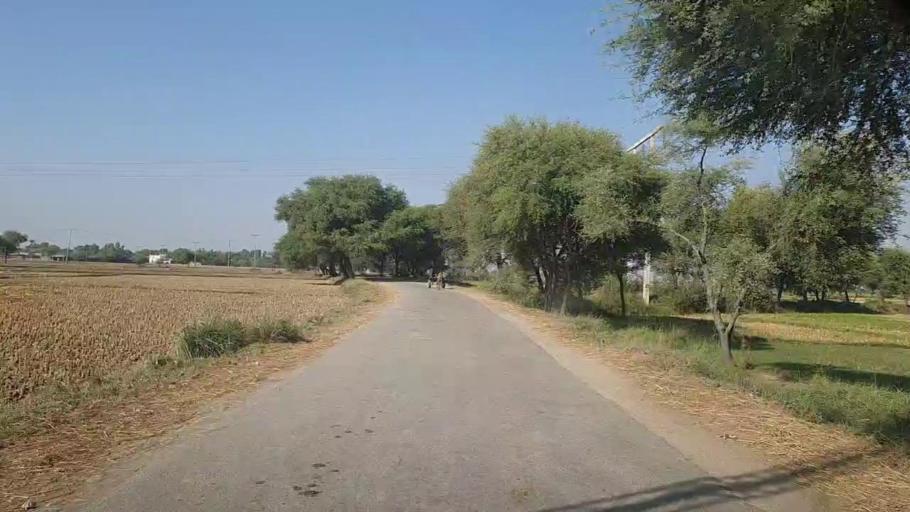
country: PK
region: Sindh
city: Tangwani
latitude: 28.2423
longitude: 68.9971
